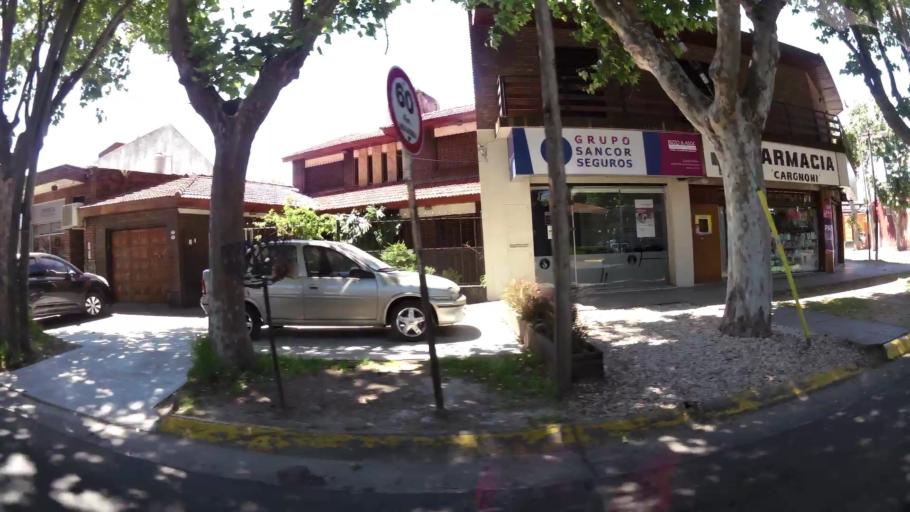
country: AR
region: Buenos Aires
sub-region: Partido de Vicente Lopez
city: Olivos
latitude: -34.5162
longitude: -58.5427
